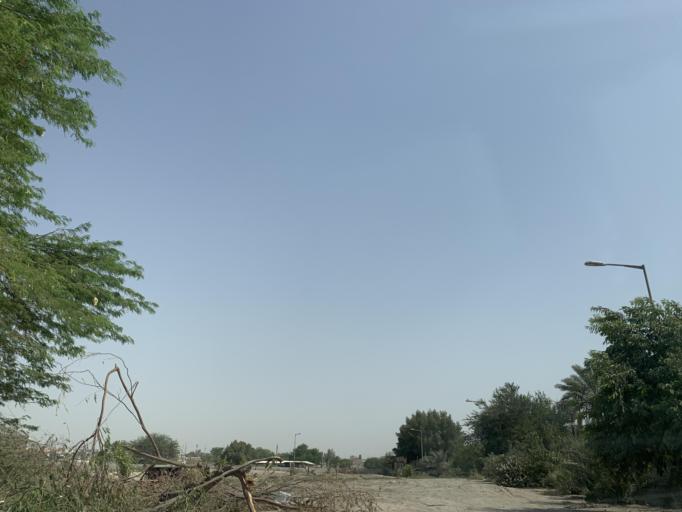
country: BH
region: Manama
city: Jidd Hafs
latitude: 26.2149
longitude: 50.5161
